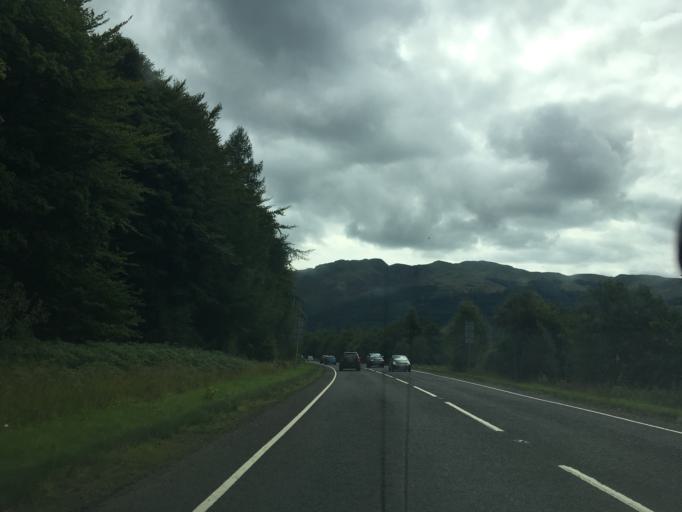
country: GB
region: Scotland
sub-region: Stirling
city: Callander
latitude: 56.3149
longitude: -4.3289
